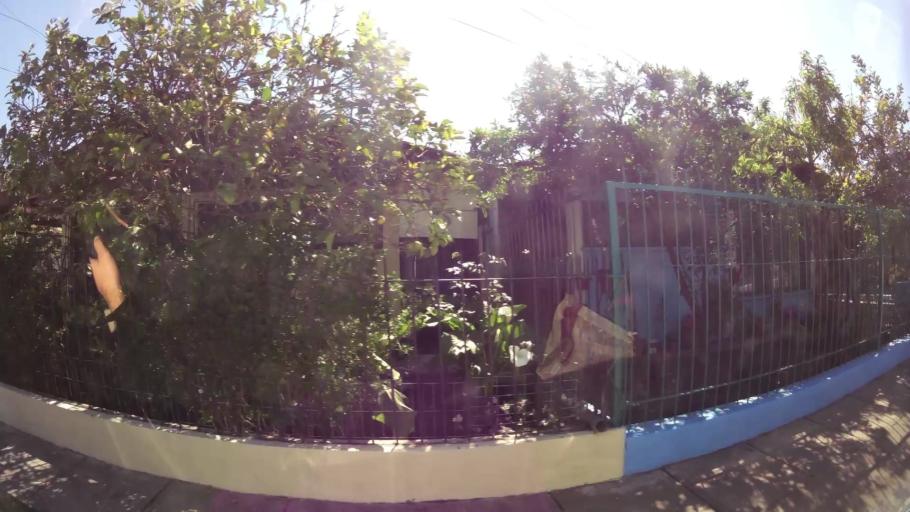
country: CL
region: Santiago Metropolitan
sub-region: Provincia de Talagante
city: Penaflor
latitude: -33.6013
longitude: -70.8882
